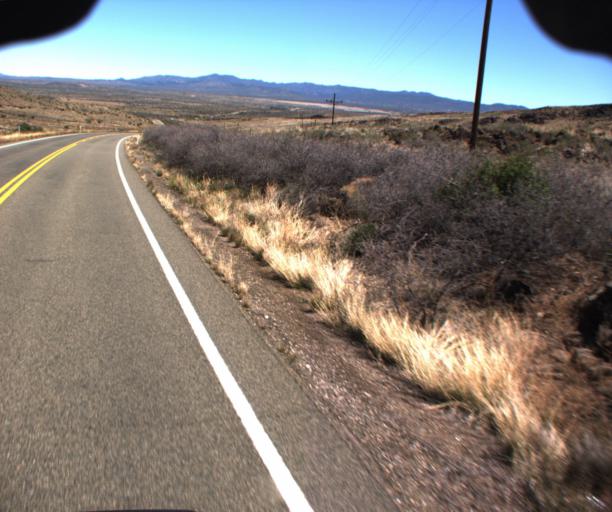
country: US
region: Arizona
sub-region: Yavapai County
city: Congress
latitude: 34.3387
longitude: -112.6861
